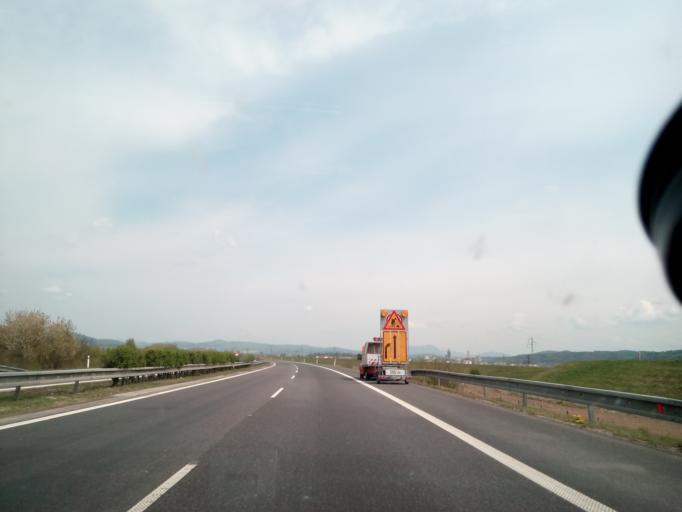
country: SK
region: Nitriansky
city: Ilava
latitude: 49.0179
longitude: 18.2550
